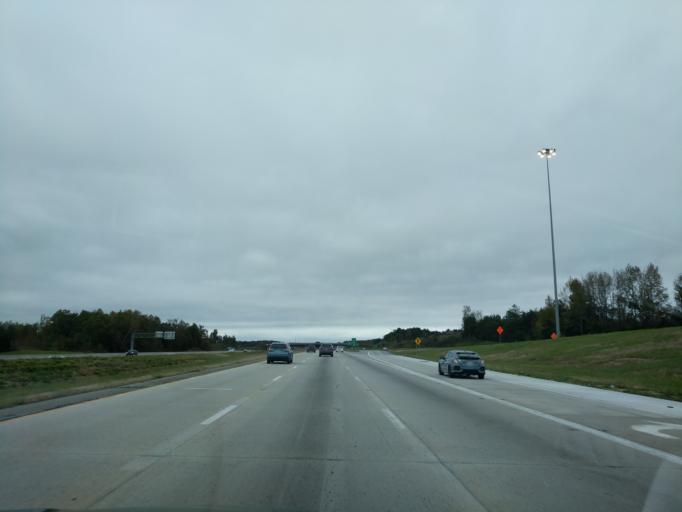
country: US
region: North Carolina
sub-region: Randolph County
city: Archdale
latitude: 35.9226
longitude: -79.9354
